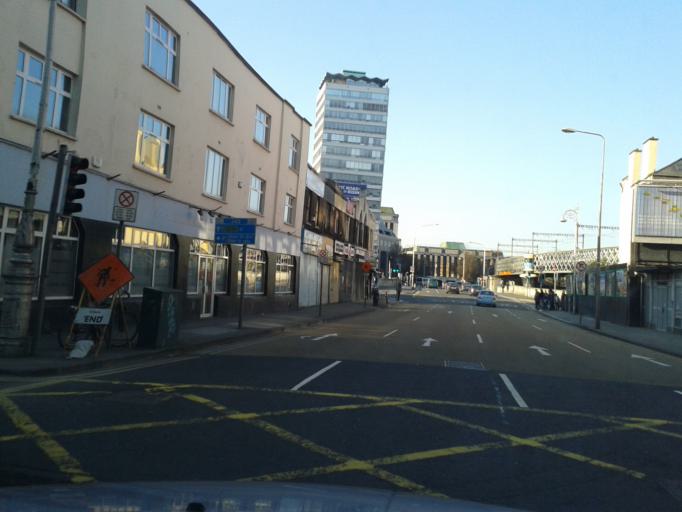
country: IE
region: Leinster
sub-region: Dublin City
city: Dublin
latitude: 53.3466
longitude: -6.2551
